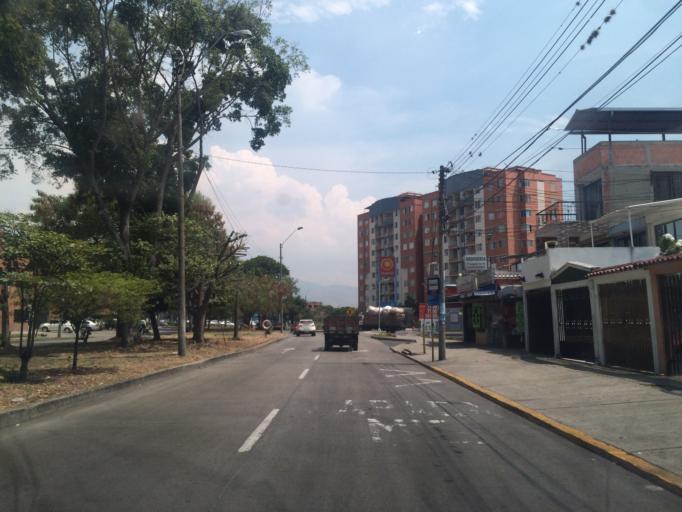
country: CO
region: Valle del Cauca
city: Cali
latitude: 3.4743
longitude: -76.5036
